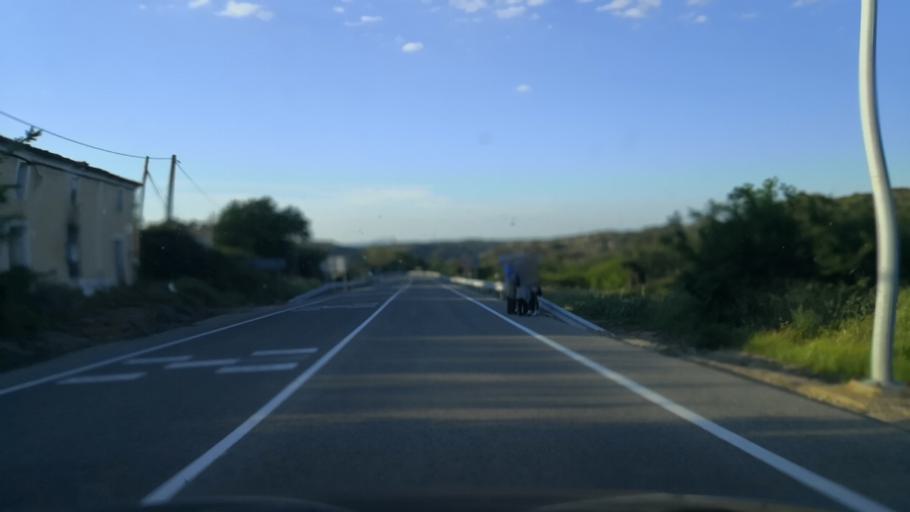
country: PT
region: Portalegre
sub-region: Portalegre
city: Sao Juliao
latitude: 39.3517
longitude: -7.2747
